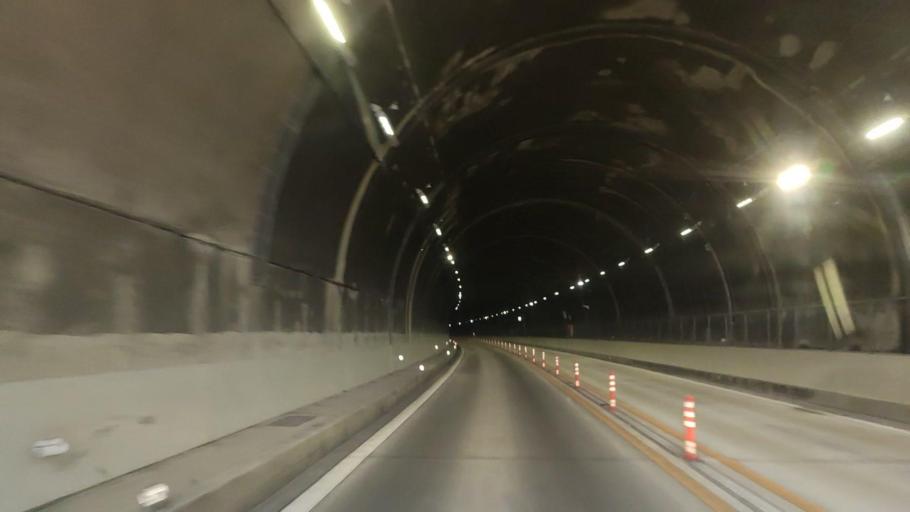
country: JP
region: Hiroshima
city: Innoshima
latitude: 34.1758
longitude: 133.0680
